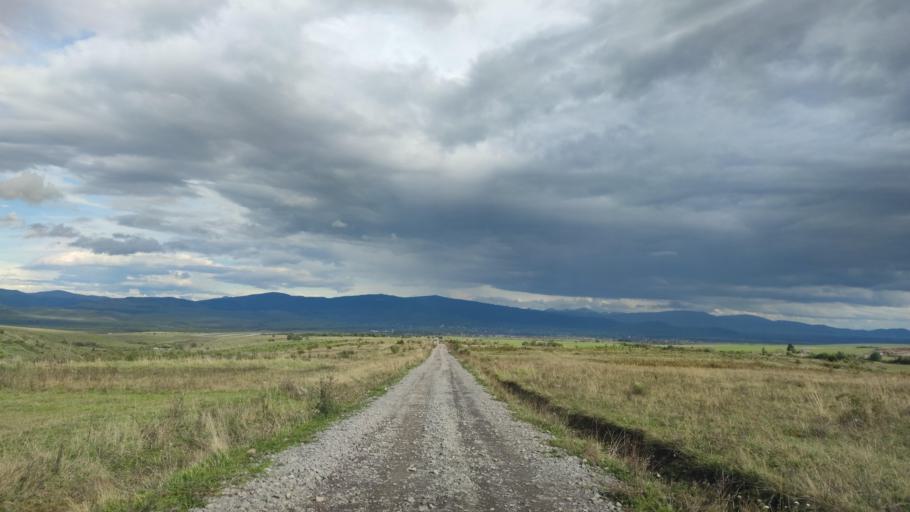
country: RO
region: Harghita
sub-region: Comuna Remetea
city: Remetea
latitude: 46.8162
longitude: 25.3718
